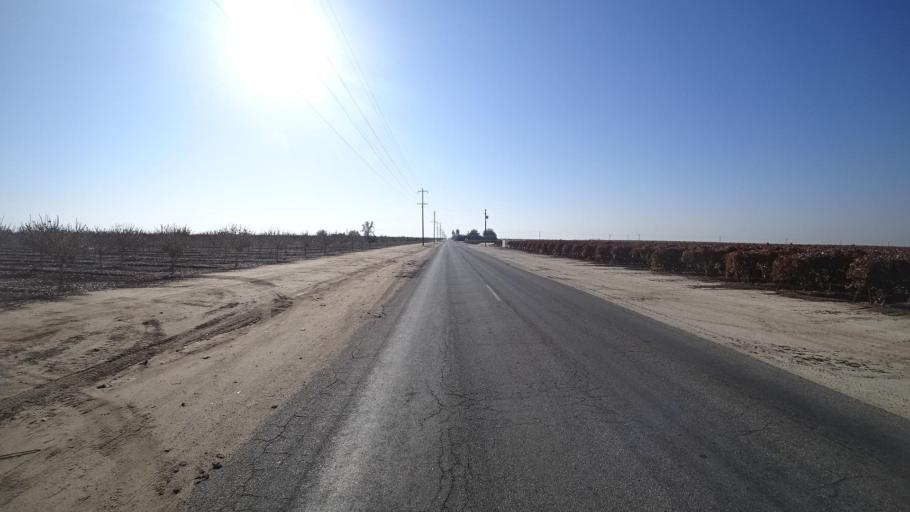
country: US
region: California
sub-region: Kern County
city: Delano
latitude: 35.7647
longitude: -119.2052
